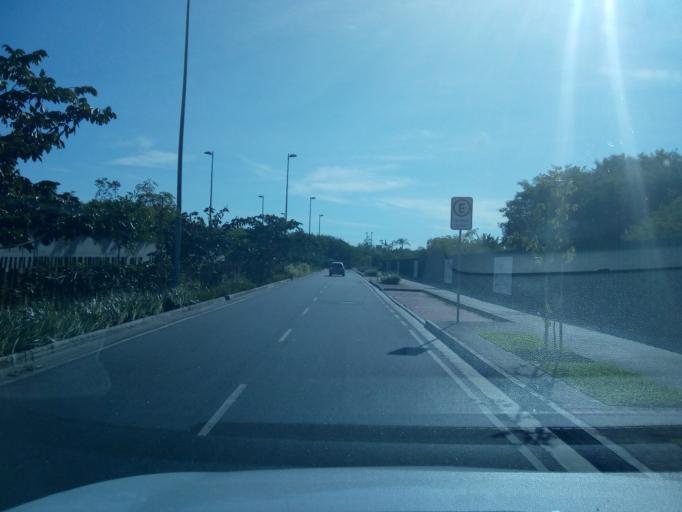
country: BR
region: Rio de Janeiro
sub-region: Nilopolis
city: Nilopolis
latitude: -23.0217
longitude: -43.5072
